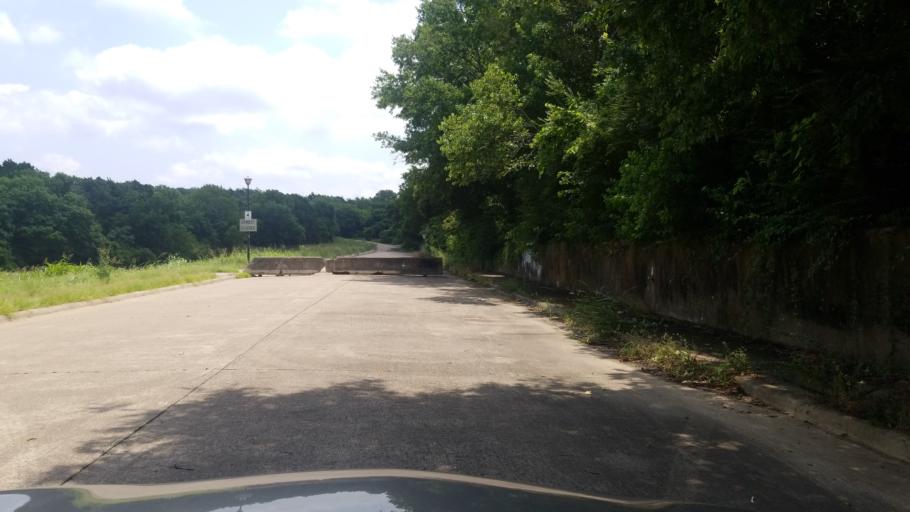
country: US
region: Texas
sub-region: Dallas County
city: Duncanville
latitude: 32.6839
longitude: -96.9230
